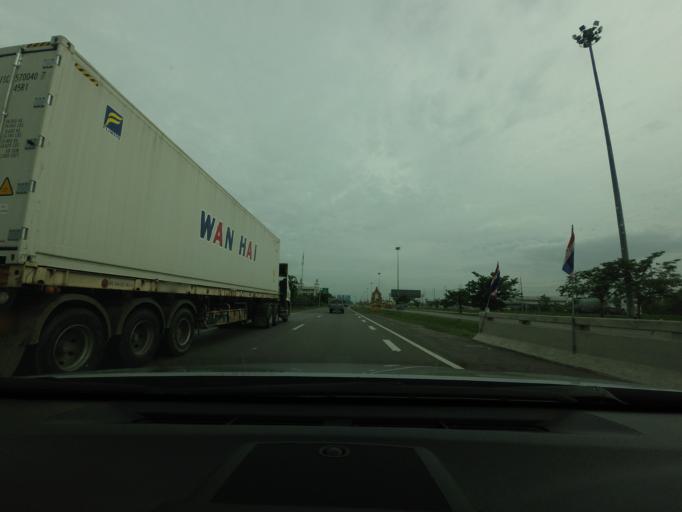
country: TH
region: Ratchaburi
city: Pak Tho
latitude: 13.3378
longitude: 99.8310
